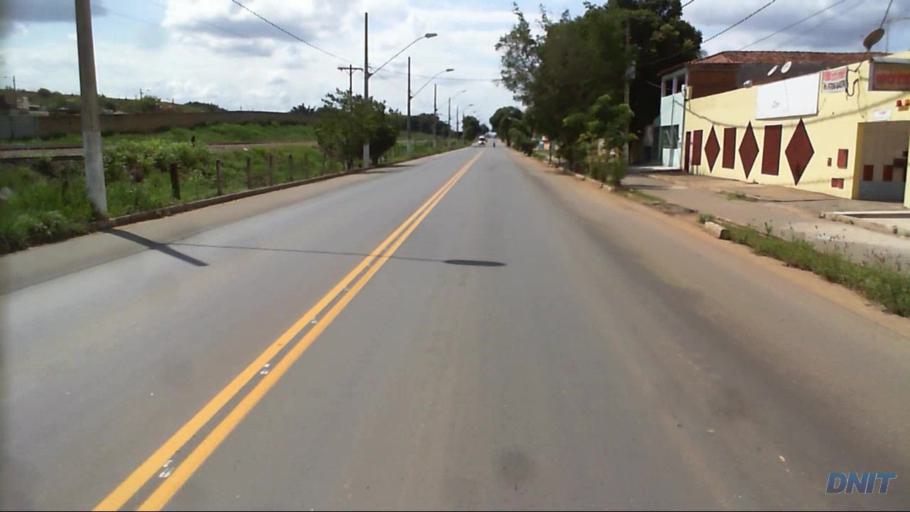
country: BR
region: Minas Gerais
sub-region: Governador Valadares
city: Governador Valadares
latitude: -18.9090
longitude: -41.9939
